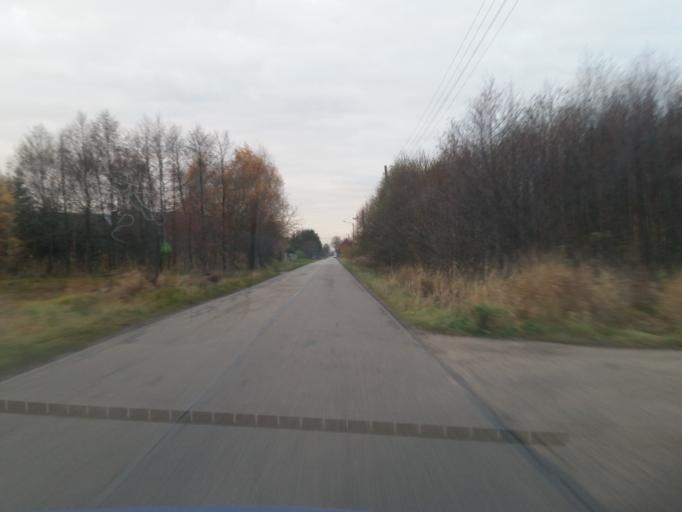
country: PL
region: Silesian Voivodeship
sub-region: Powiat czestochowski
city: Borowno
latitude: 50.9621
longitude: 19.2700
